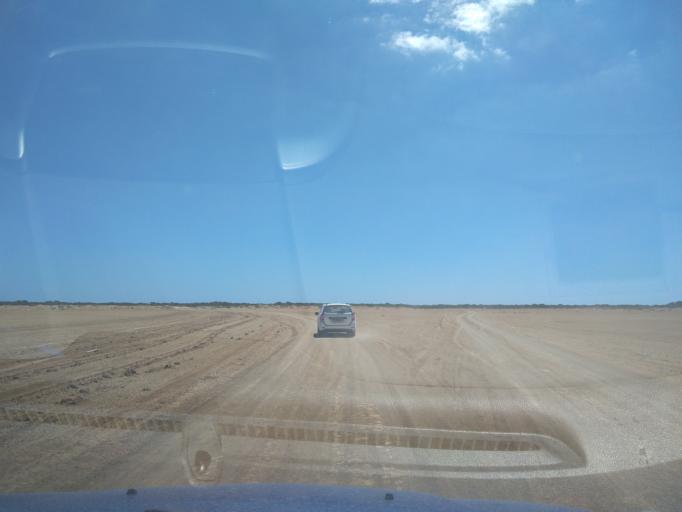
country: TN
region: Susah
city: Harqalah
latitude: 36.1623
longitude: 10.4562
